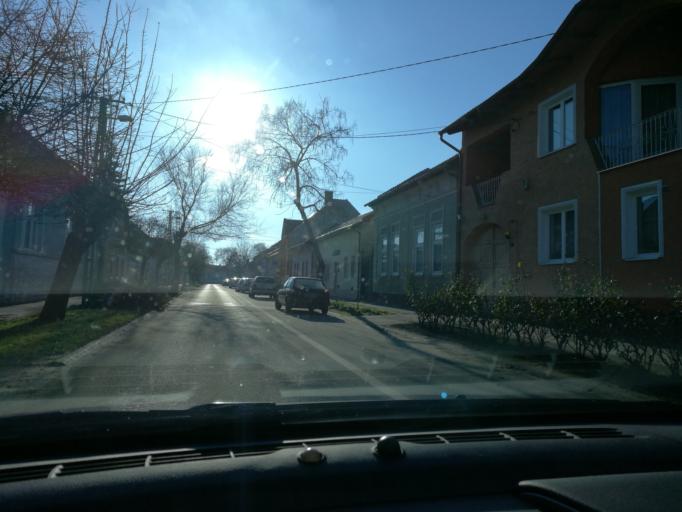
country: HU
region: Szabolcs-Szatmar-Bereg
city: Nyiregyhaza
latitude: 47.9572
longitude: 21.7100
